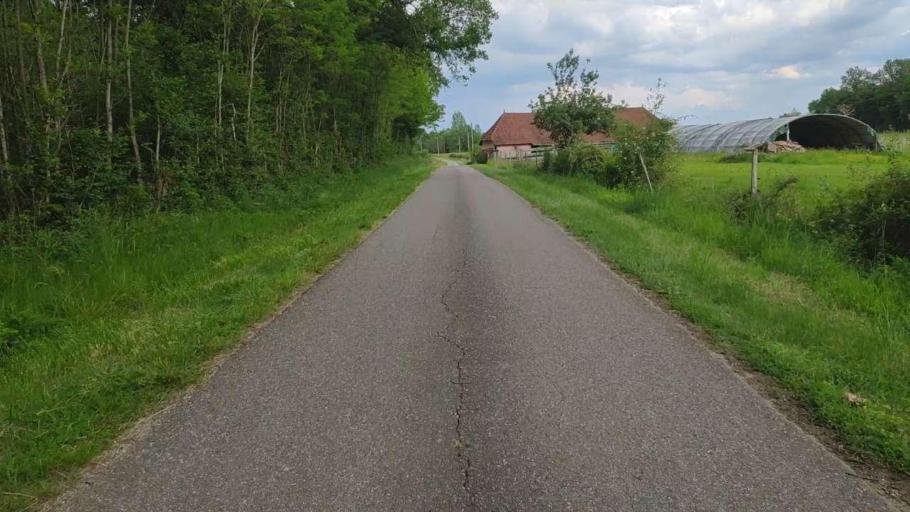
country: FR
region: Franche-Comte
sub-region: Departement du Jura
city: Bletterans
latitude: 46.7949
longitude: 5.3556
